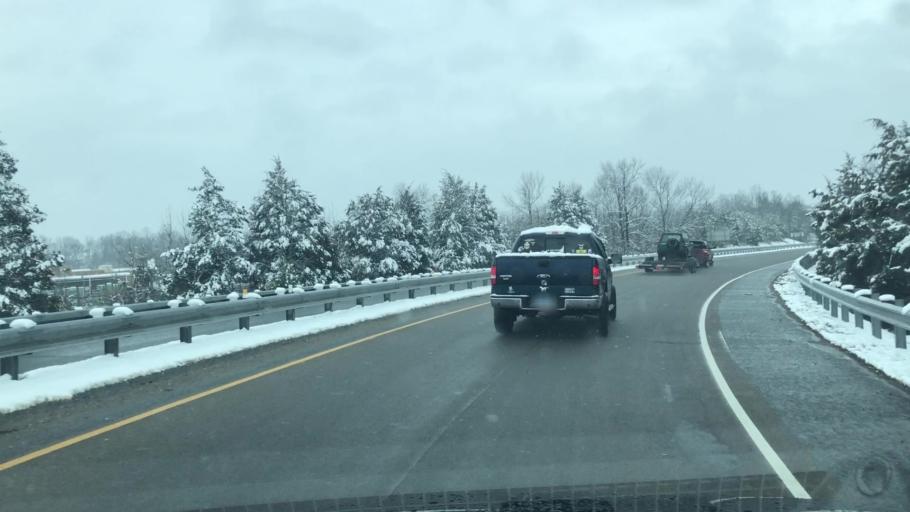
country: US
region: Virginia
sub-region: City of Fredericksburg
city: Fredericksburg
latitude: 38.2951
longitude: -77.5031
